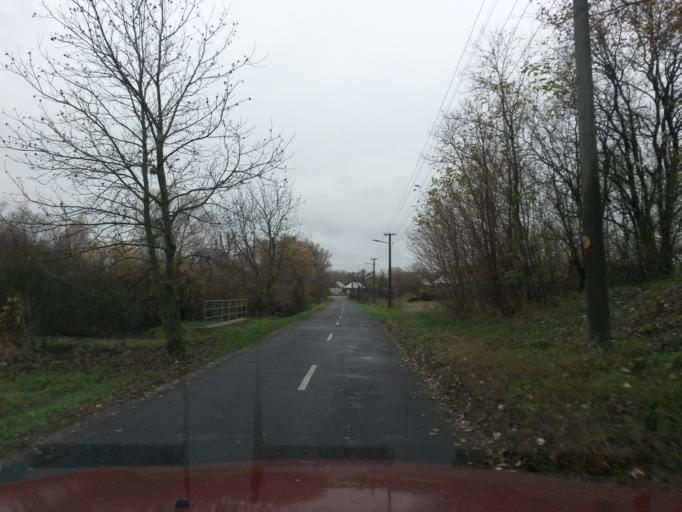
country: SK
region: Kosicky
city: Cierna nad Tisou
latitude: 48.5544
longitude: 21.9552
